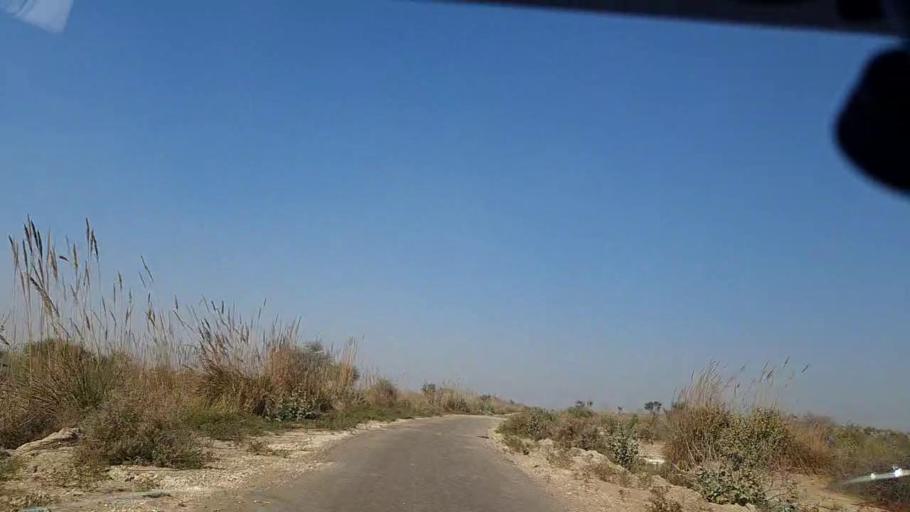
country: PK
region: Sindh
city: Khanpur
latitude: 27.5807
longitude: 69.3769
